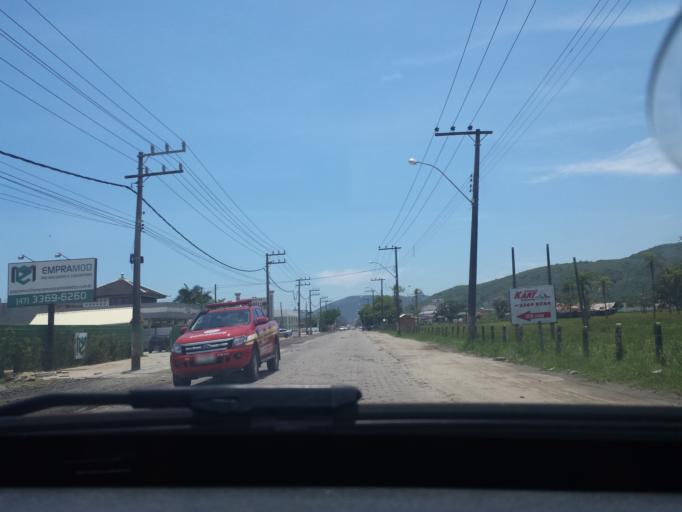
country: BR
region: Santa Catarina
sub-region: Porto Belo
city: Porto Belo
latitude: -27.1608
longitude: -48.5767
